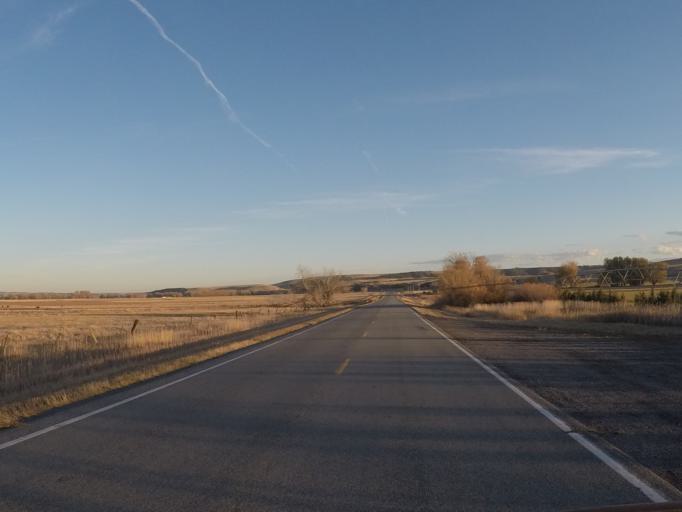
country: US
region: Montana
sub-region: Sweet Grass County
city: Big Timber
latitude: 45.8001
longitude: -109.8621
